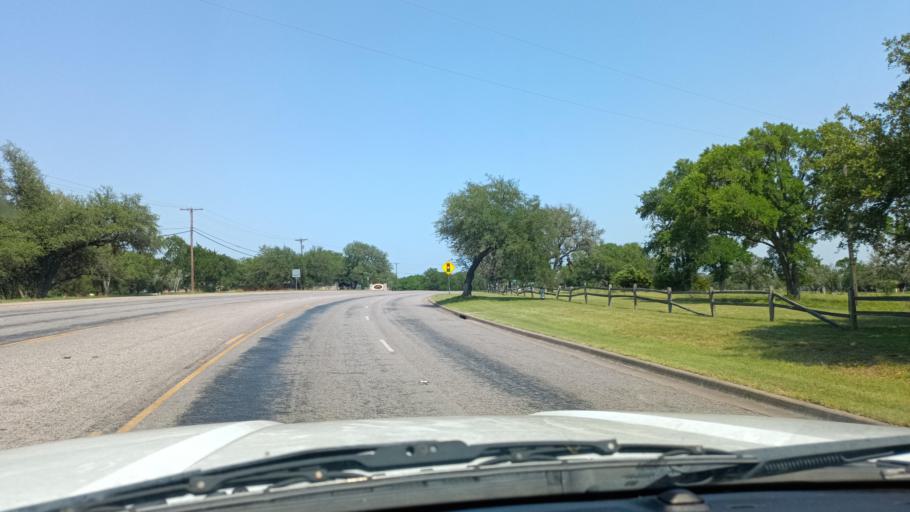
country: US
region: Texas
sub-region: Bell County
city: Morgans Point Resort
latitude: 31.1038
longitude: -97.4807
